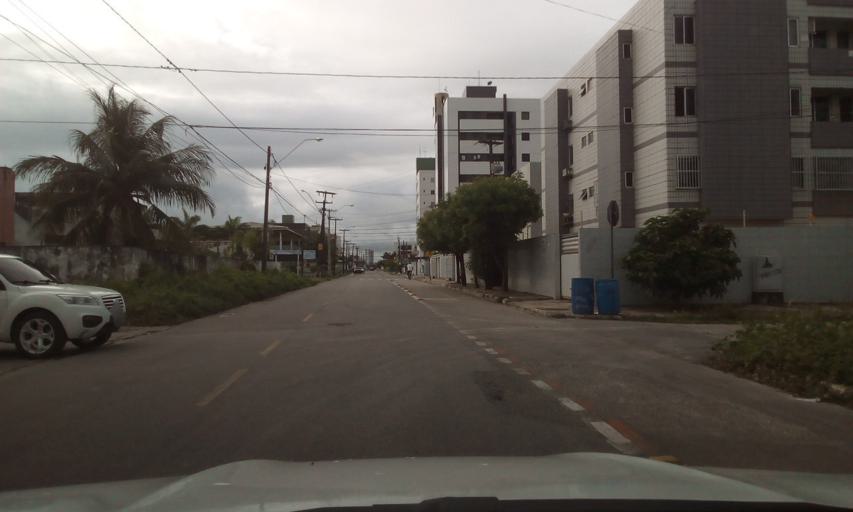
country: BR
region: Paraiba
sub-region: Joao Pessoa
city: Joao Pessoa
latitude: -7.0726
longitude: -34.8423
